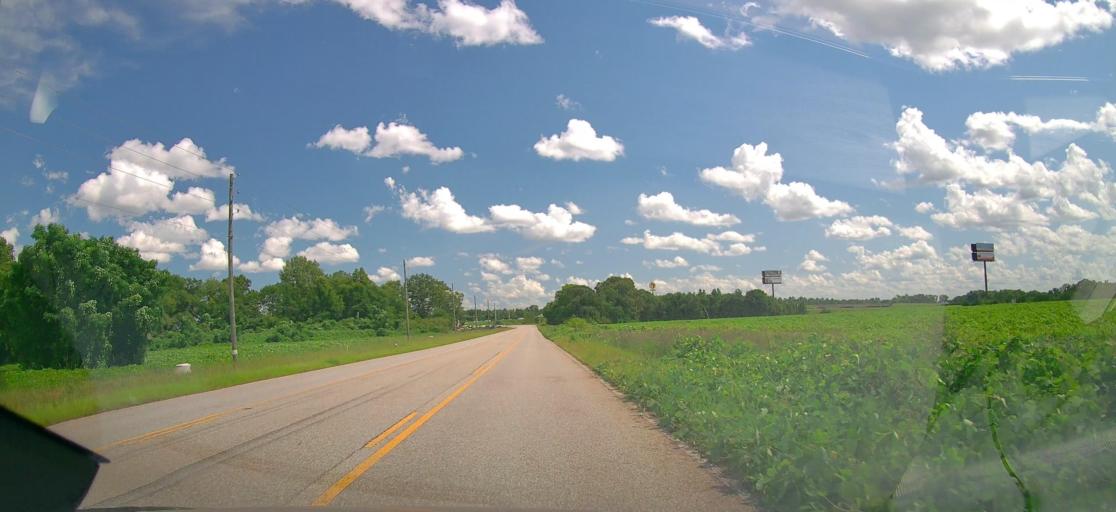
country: US
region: Georgia
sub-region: Houston County
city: Centerville
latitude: 32.5923
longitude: -83.7392
